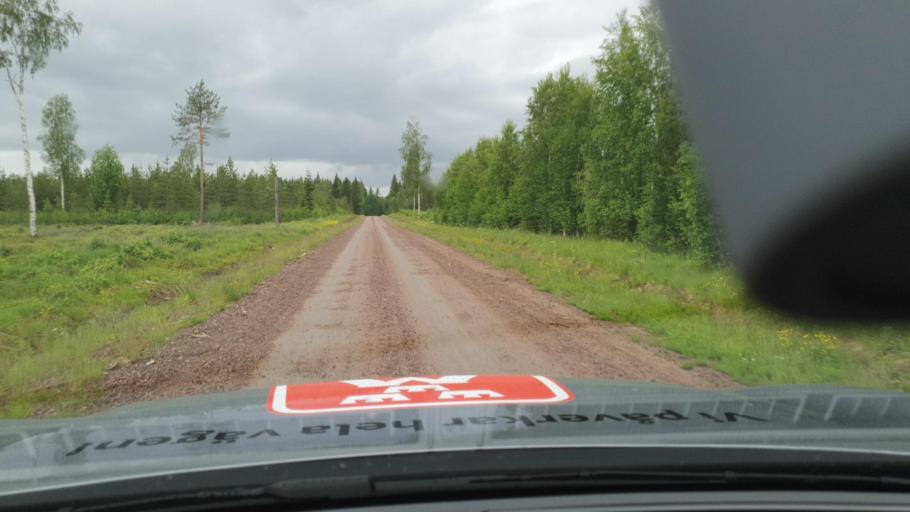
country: SE
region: Norrbotten
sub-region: Overkalix Kommun
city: OEverkalix
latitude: 66.6111
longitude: 22.7395
